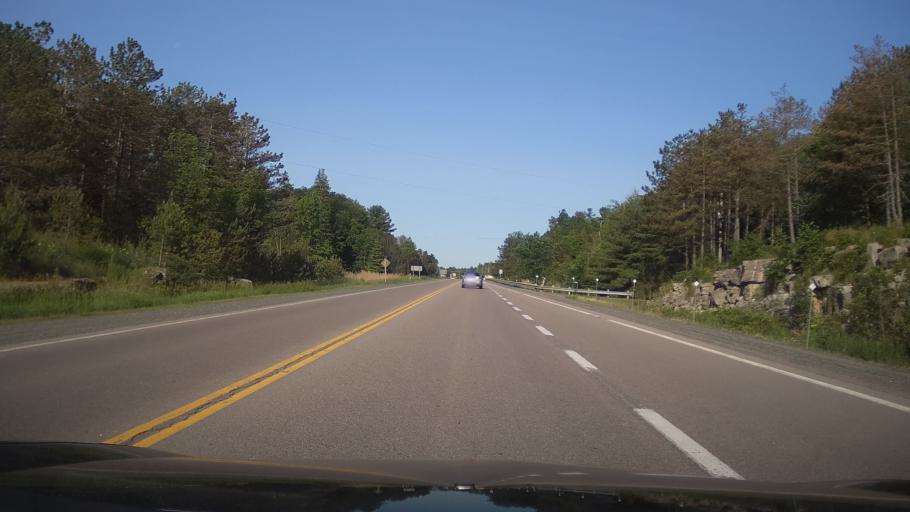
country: CA
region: Ontario
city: Quinte West
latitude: 44.4884
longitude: -77.6654
